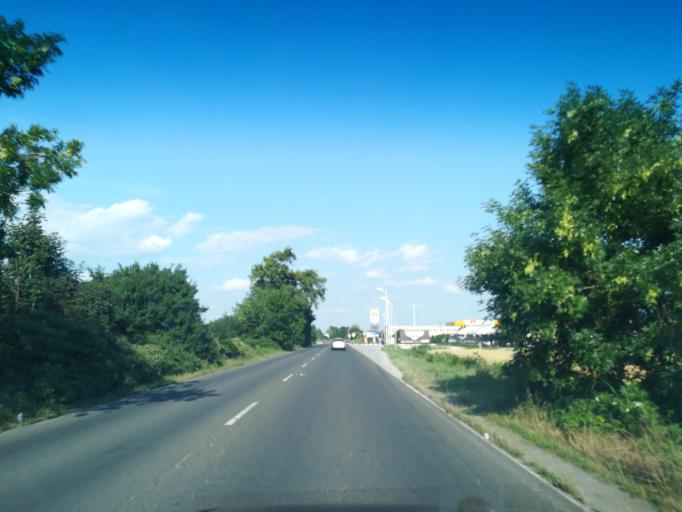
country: BG
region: Plovdiv
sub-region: Obshtina Plovdiv
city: Plovdiv
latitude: 42.1489
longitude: 24.8259
